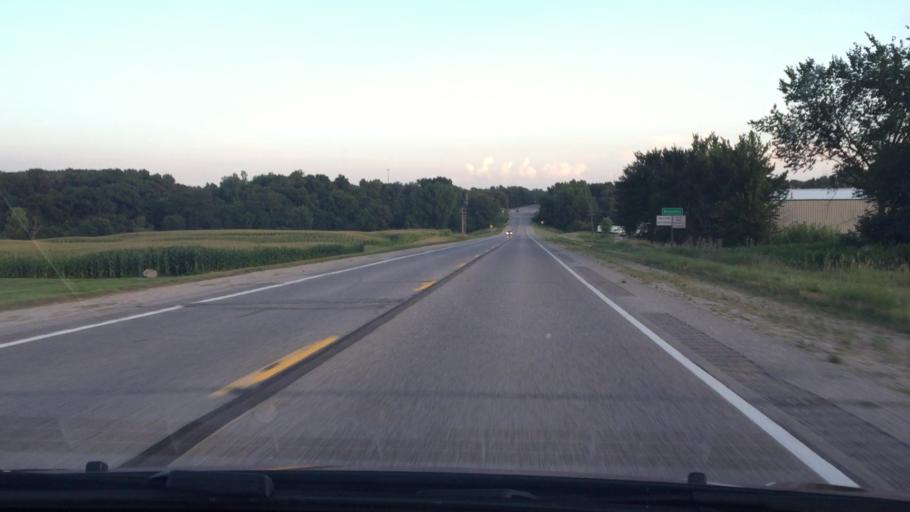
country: US
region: Iowa
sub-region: Muscatine County
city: Muscatine
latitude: 41.4648
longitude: -91.0339
